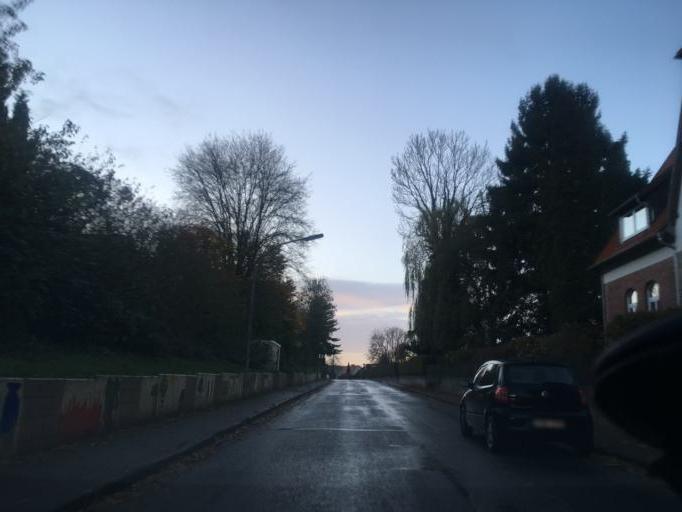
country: DE
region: Lower Saxony
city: Uslar
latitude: 51.6251
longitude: 9.6195
